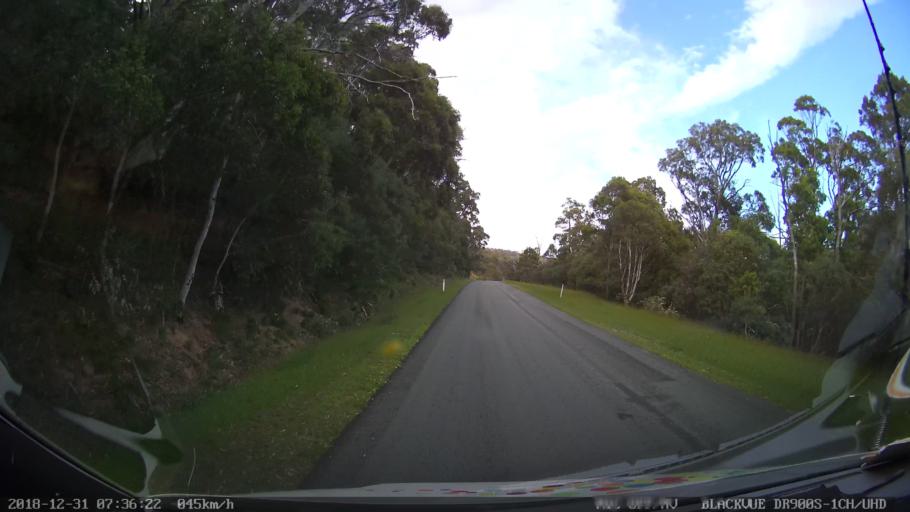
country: AU
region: New South Wales
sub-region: Snowy River
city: Jindabyne
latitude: -36.3405
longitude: 148.4431
